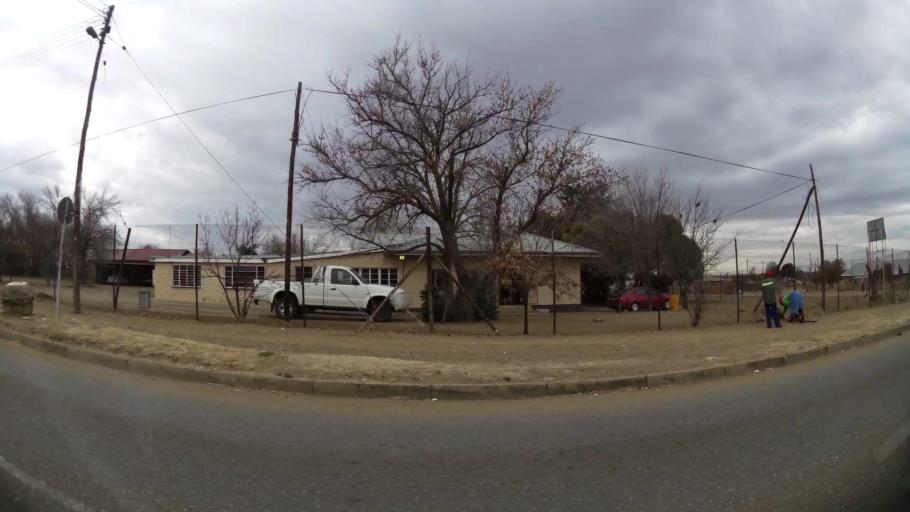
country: ZA
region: Orange Free State
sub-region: Fezile Dabi District Municipality
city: Kroonstad
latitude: -27.6535
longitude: 27.2093
